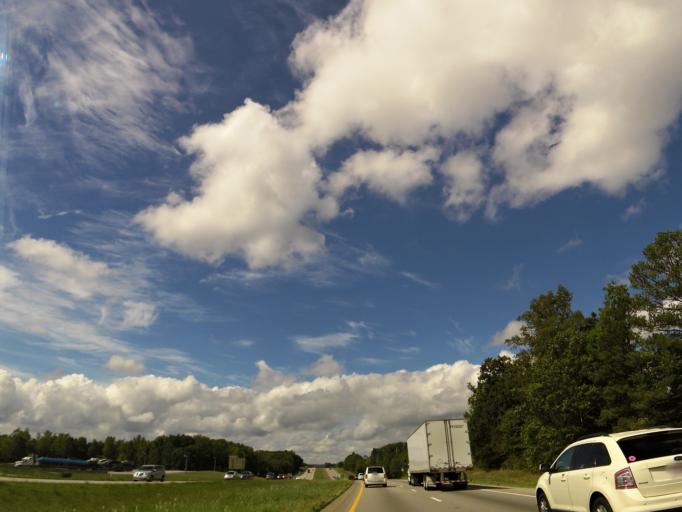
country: US
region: Tennessee
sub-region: Bradley County
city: Cleveland
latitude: 35.1847
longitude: -84.9068
